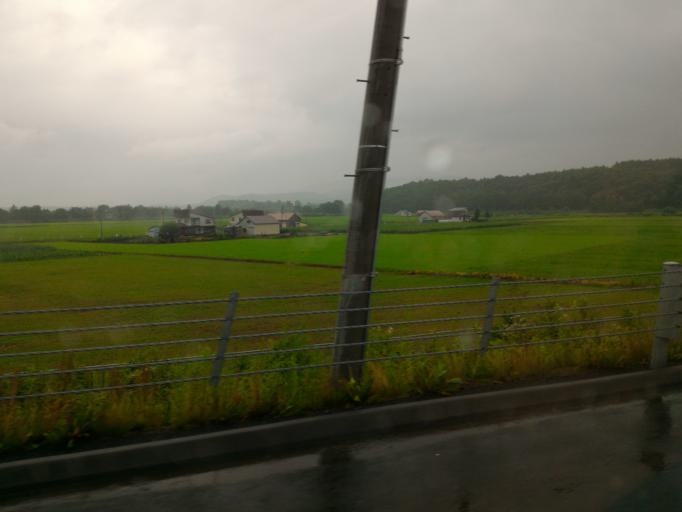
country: JP
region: Hokkaido
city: Nayoro
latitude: 44.4941
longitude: 142.3497
